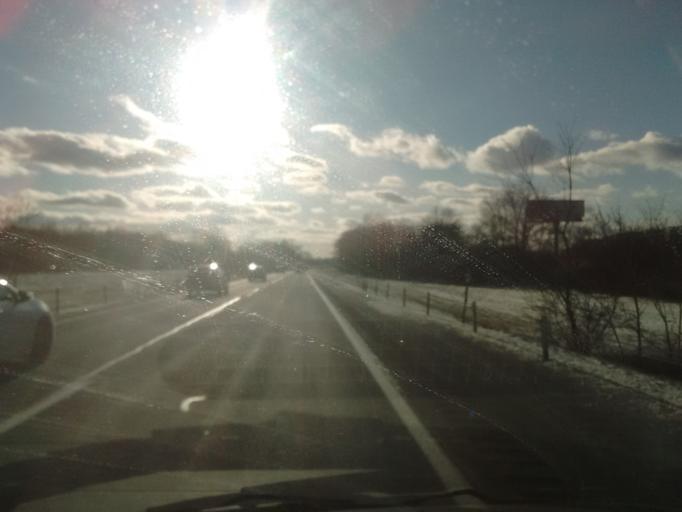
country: US
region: New York
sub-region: Orange County
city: Scotchtown
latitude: 41.4573
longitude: -74.3524
